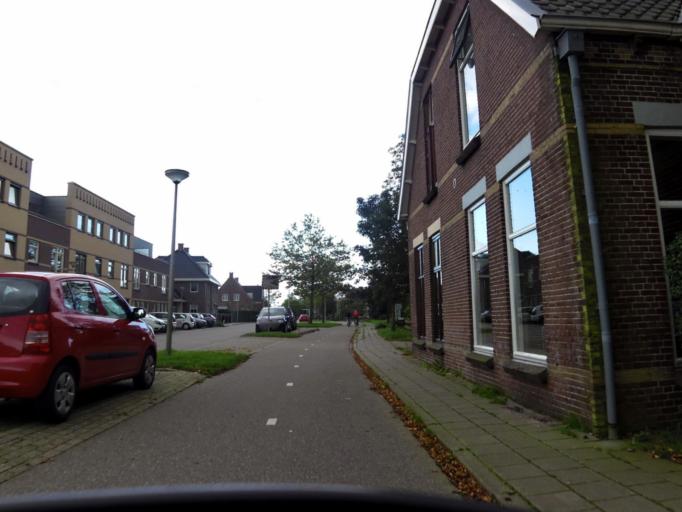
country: NL
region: South Holland
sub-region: Gemeente Leiderdorp
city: Leiderdorp
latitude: 52.1288
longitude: 4.5672
